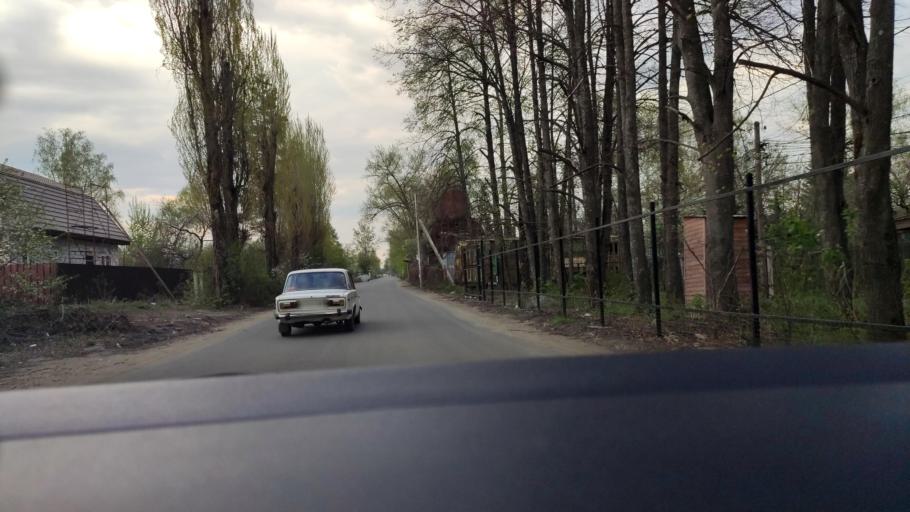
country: RU
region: Voronezj
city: Voronezh
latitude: 51.6019
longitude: 39.1620
